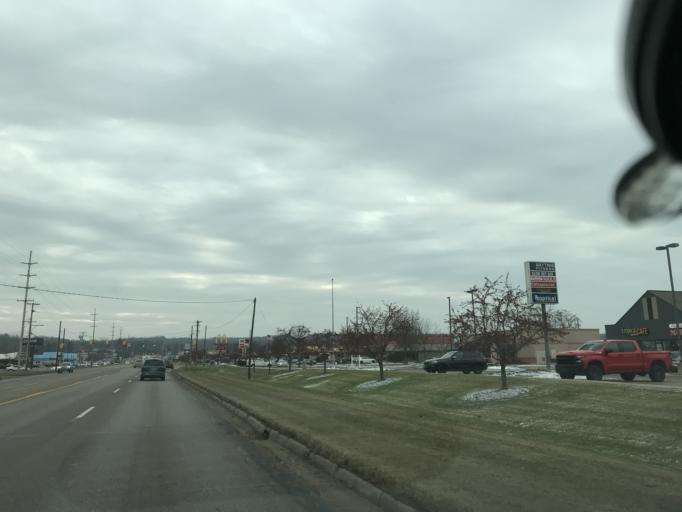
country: US
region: Michigan
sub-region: Kent County
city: Northview
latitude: 43.0614
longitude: -85.5800
